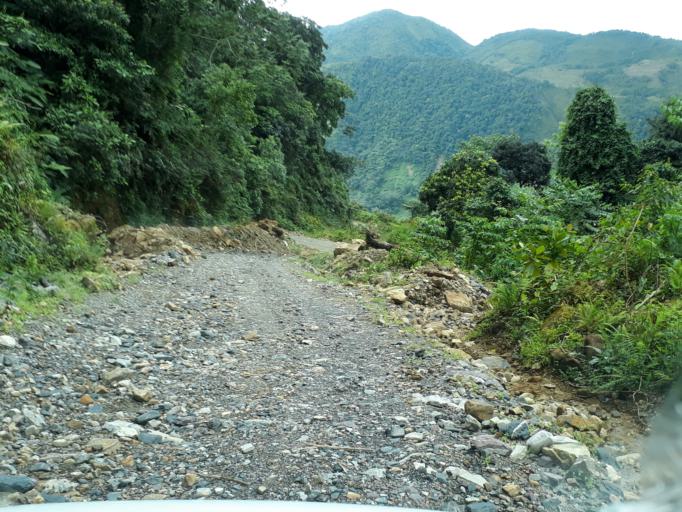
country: CO
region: Cundinamarca
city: Gachala
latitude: 4.7095
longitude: -73.3715
